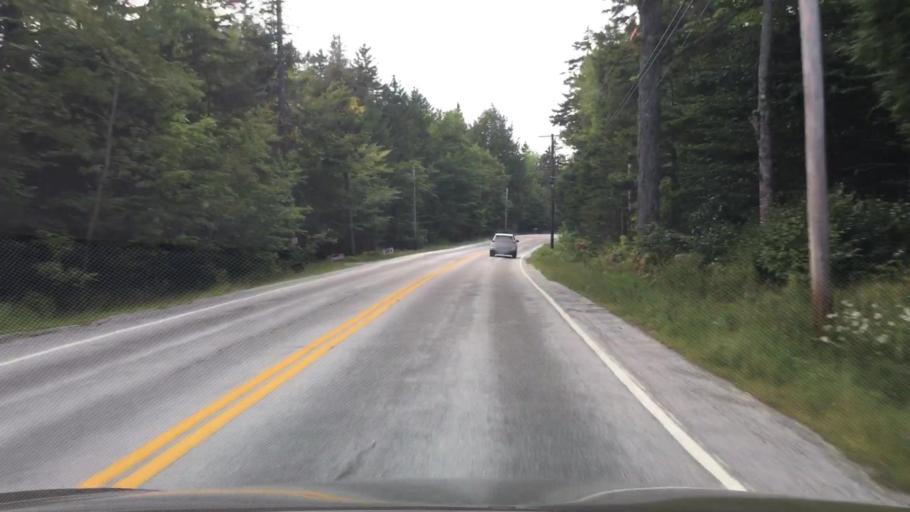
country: US
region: Maine
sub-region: Hancock County
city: Penobscot
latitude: 44.4274
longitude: -68.6025
